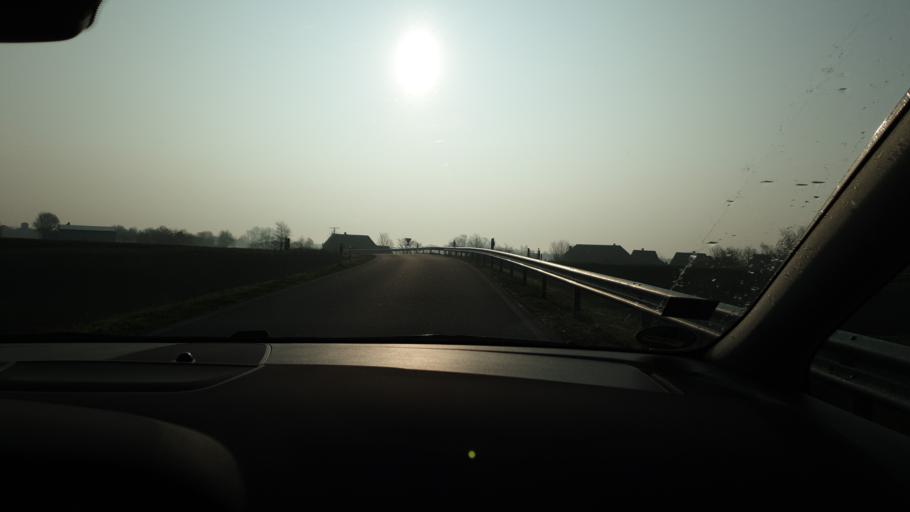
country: DE
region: Schleswig-Holstein
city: Elisabeth-Sophien-Koog
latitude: 54.4961
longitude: 8.9110
